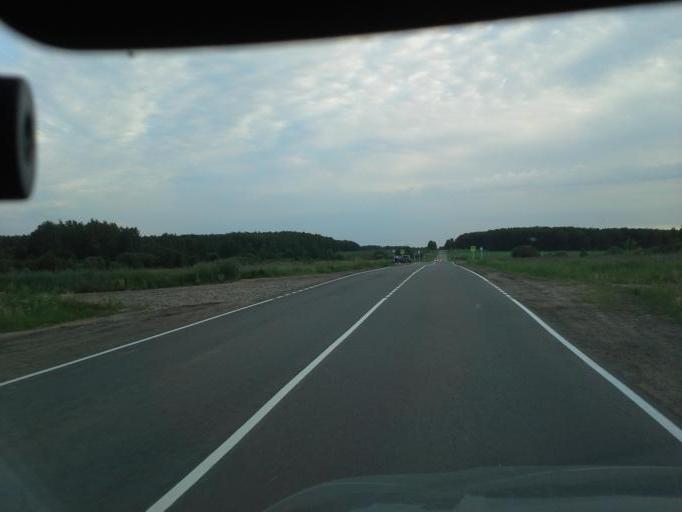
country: RU
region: Ivanovo
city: Petrovskiy
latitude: 56.6048
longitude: 40.2516
